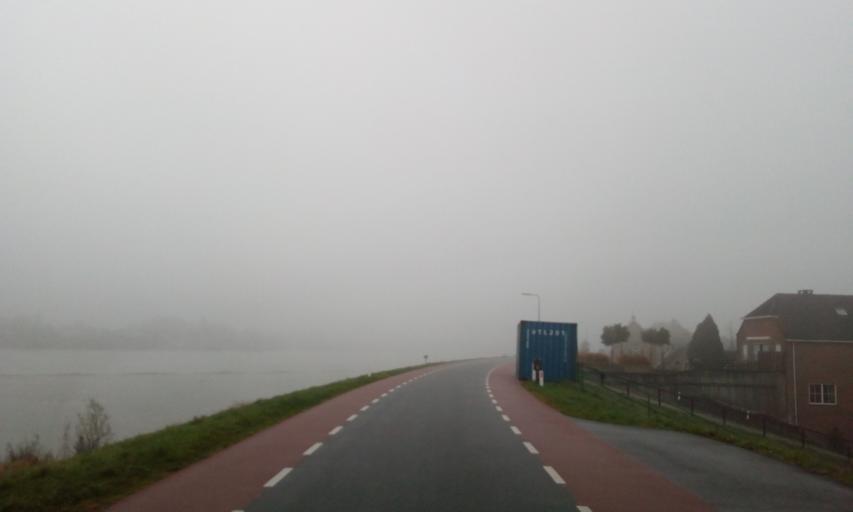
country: NL
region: South Holland
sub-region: Molenwaard
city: Liesveld
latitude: 51.9282
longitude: 4.8134
